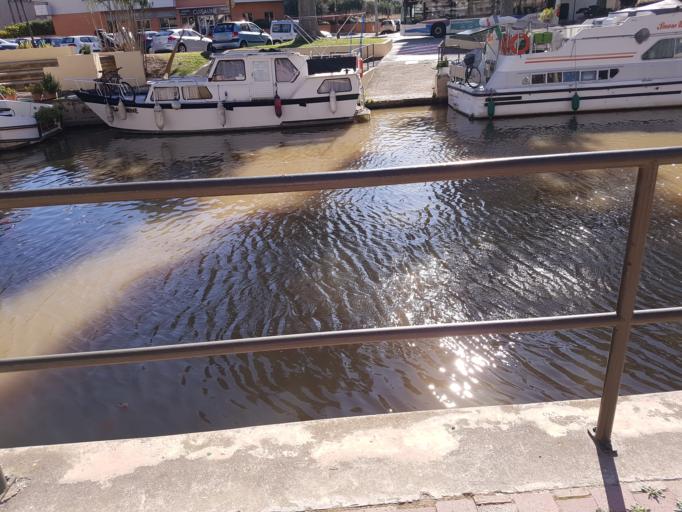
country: FR
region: Languedoc-Roussillon
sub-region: Departement de l'Aude
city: Narbonne
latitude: 43.1802
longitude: 3.0116
